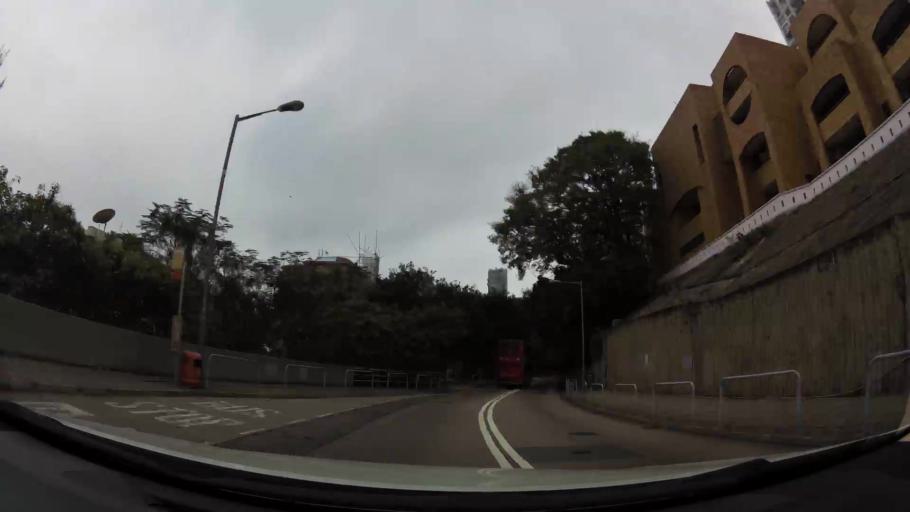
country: HK
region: Central and Western
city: Central
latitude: 22.2723
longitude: 114.1207
